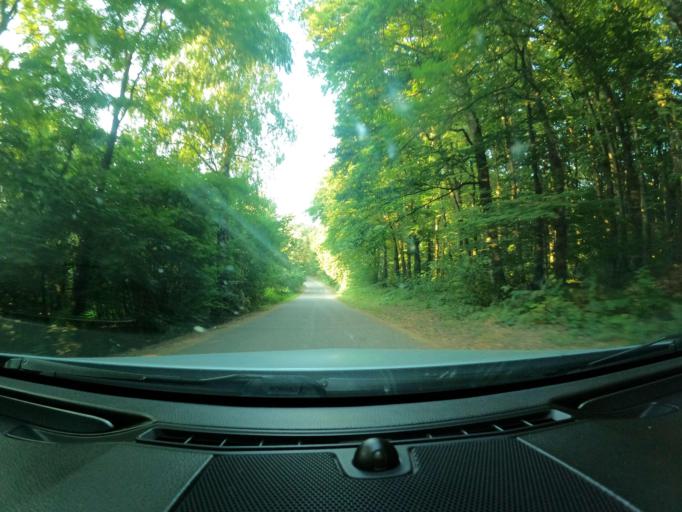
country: RS
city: Vrdnik
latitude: 45.1586
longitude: 19.7558
